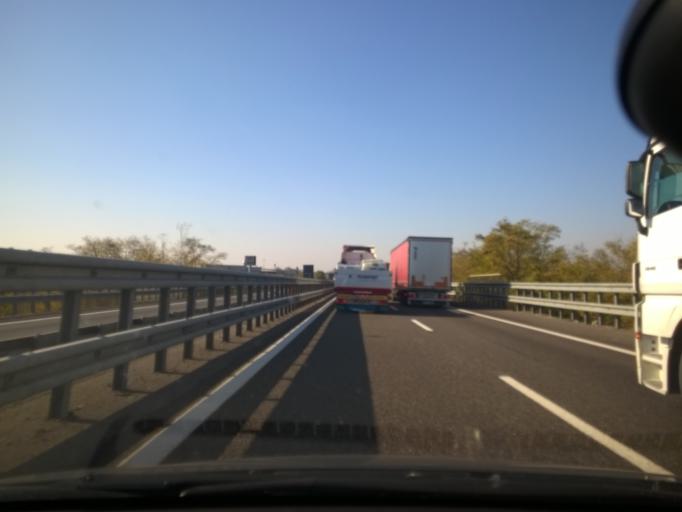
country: IT
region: Emilia-Romagna
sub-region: Provincia di Piacenza
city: San Nicolo
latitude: 45.0622
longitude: 9.6360
